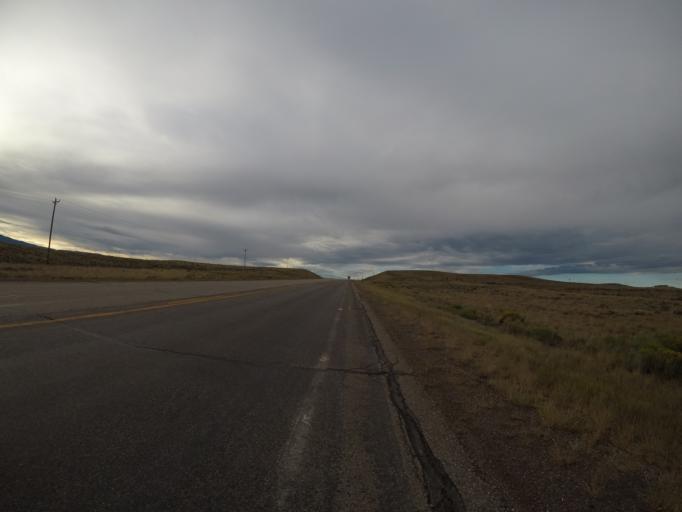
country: US
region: Wyoming
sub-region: Carbon County
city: Saratoga
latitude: 41.4252
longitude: -106.7962
